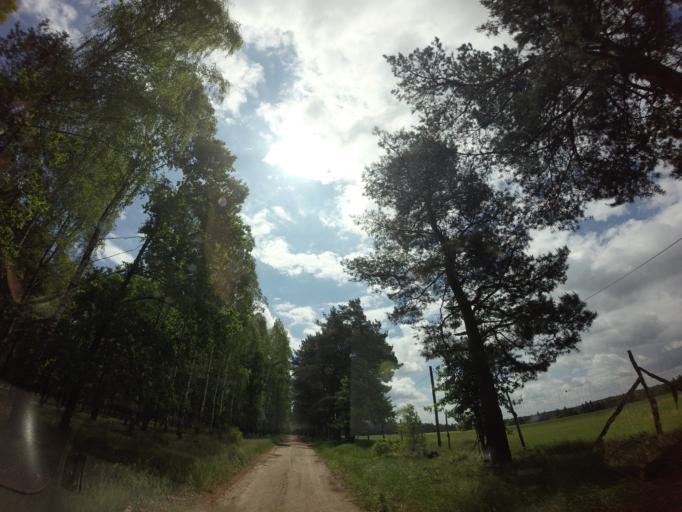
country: PL
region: West Pomeranian Voivodeship
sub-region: Powiat choszczenski
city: Drawno
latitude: 53.1828
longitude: 15.8675
